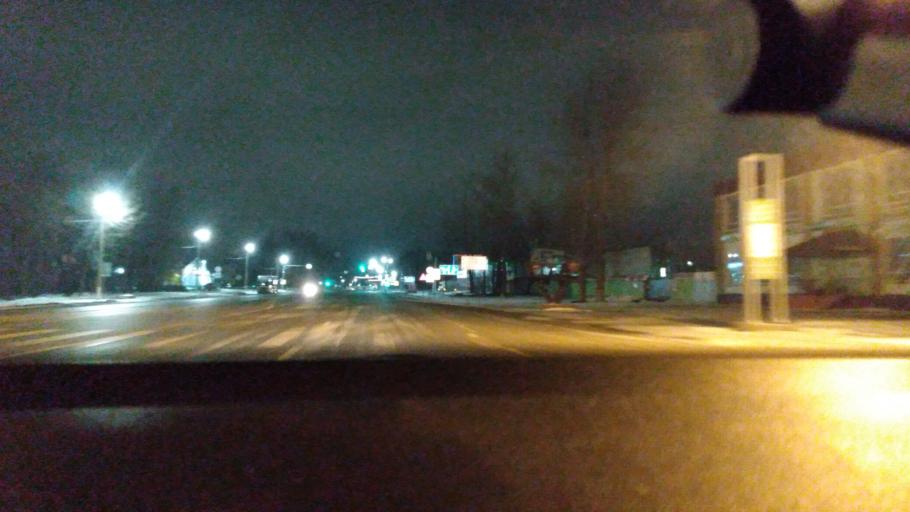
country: RU
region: Moskovskaya
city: Bronnitsy
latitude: 55.4143
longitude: 38.2857
